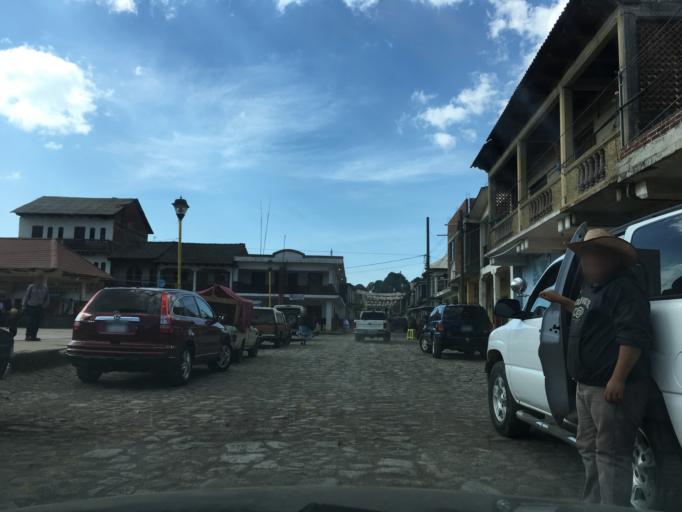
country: MX
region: Michoacan
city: Angahuan
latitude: 19.5478
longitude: -102.2249
